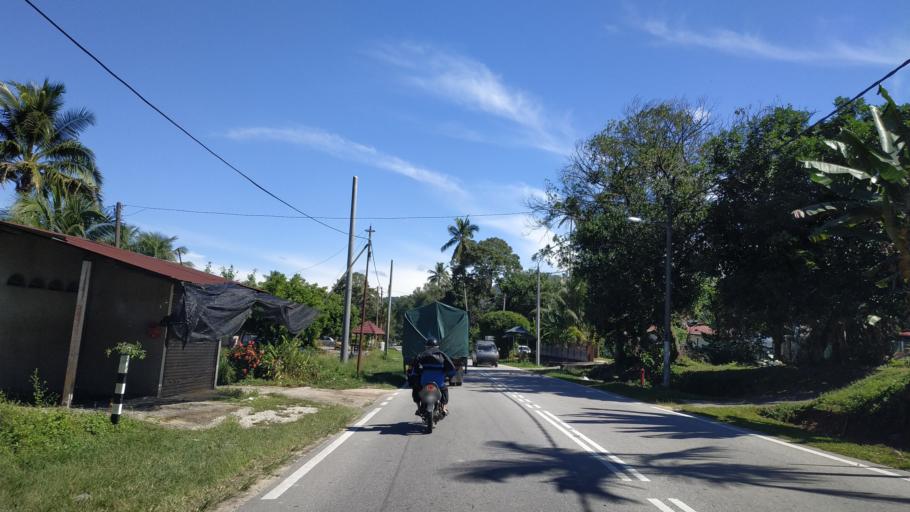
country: MY
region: Kedah
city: Kulim
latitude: 5.3073
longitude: 100.5398
